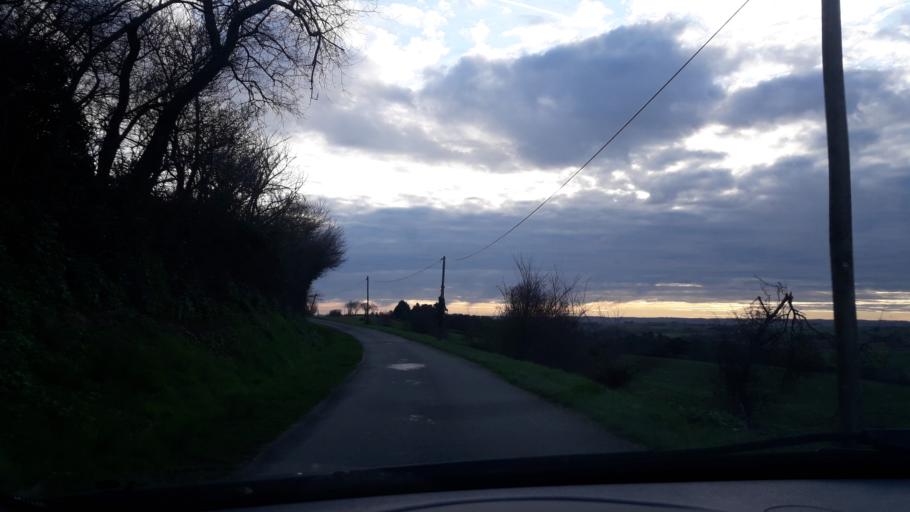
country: FR
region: Midi-Pyrenees
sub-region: Departement du Gers
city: Pujaudran
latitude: 43.6678
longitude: 1.0429
